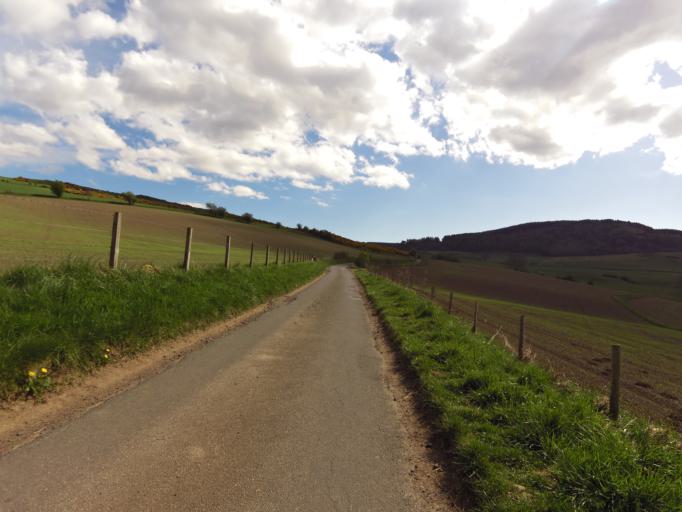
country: GB
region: Scotland
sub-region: Fife
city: Newburgh
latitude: 56.3422
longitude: -3.2529
